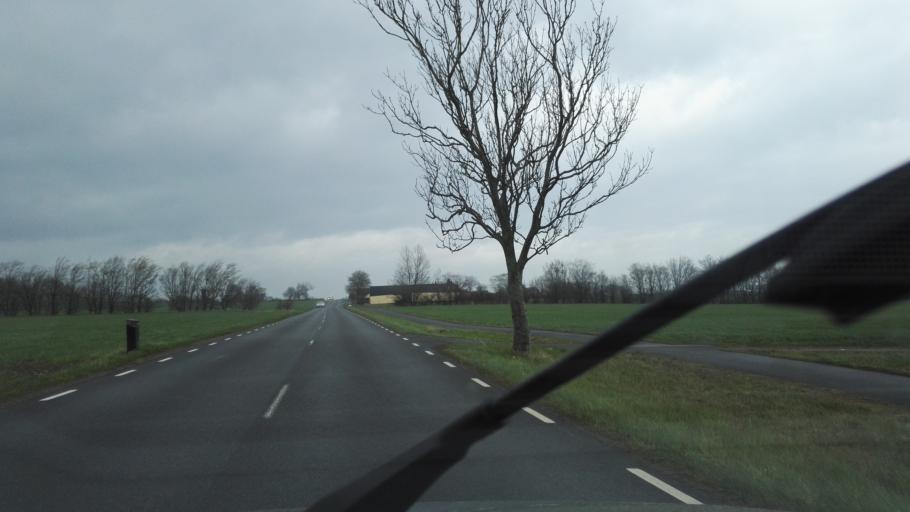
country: SE
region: Skane
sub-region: Simrishamns Kommun
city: Simrishamn
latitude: 55.4856
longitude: 14.2928
